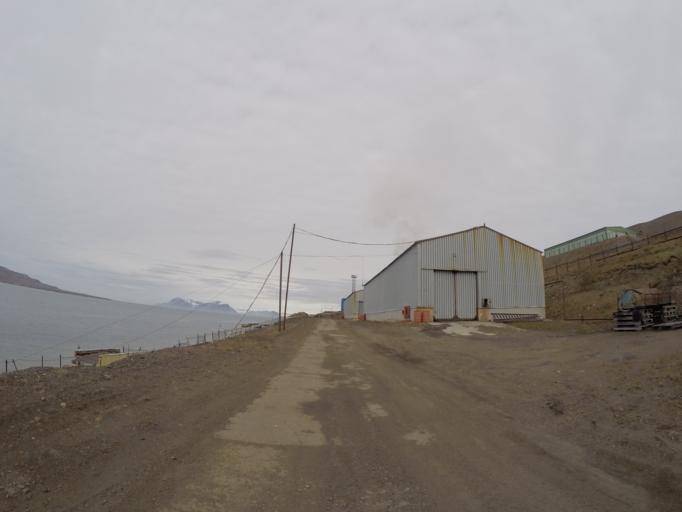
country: SJ
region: Svalbard
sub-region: Spitsbergen
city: Longyearbyen
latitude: 78.0523
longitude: 14.2125
